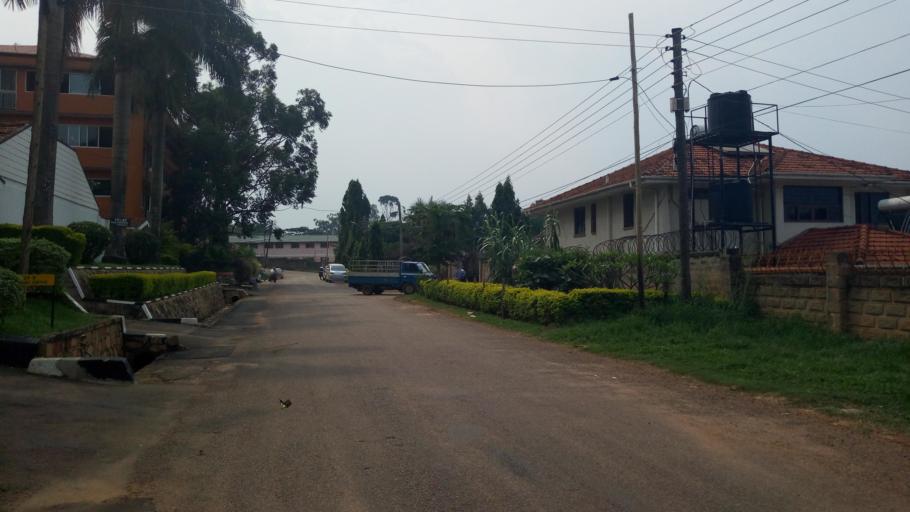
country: UG
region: Central Region
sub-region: Wakiso District
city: Kireka
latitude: 0.3117
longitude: 32.6280
